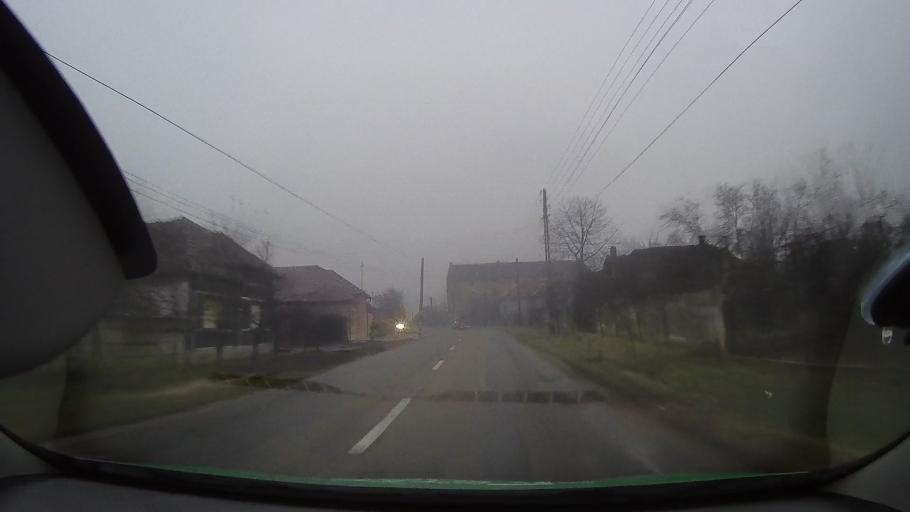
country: RO
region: Bihor
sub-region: Comuna Tulca
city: Tulca
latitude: 46.7863
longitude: 21.7847
